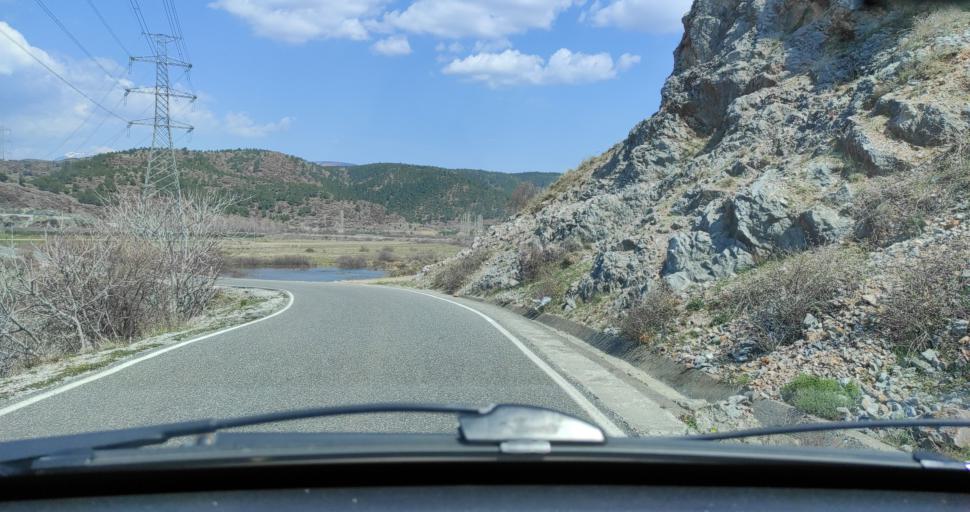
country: AL
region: Shkoder
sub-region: Rrethi i Shkodres
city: Hajmel
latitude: 41.9736
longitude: 19.6444
